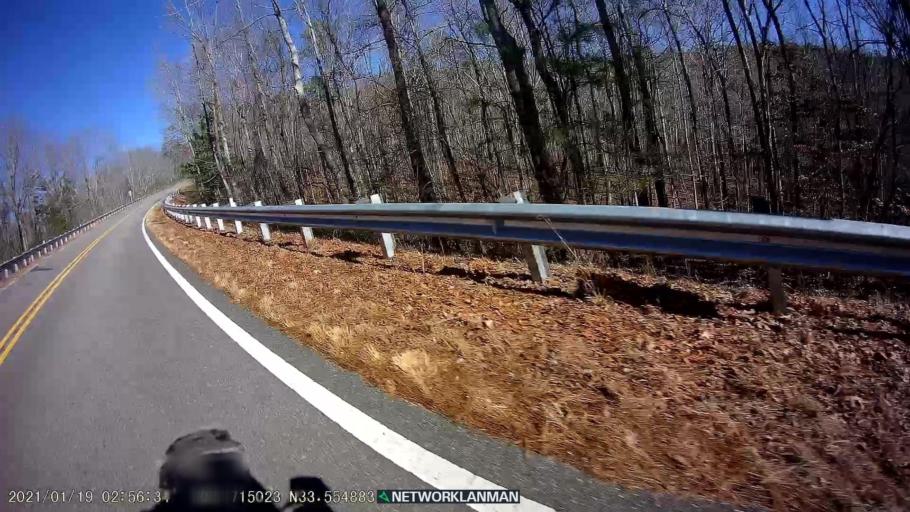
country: US
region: Alabama
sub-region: Calhoun County
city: Choccolocco
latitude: 33.5551
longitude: -85.7150
